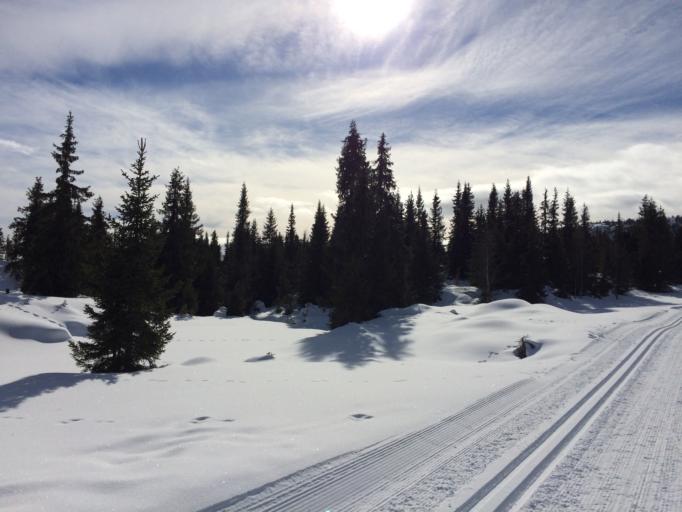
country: NO
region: Oppland
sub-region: Gausdal
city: Segalstad bru
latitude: 61.3356
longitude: 10.0607
